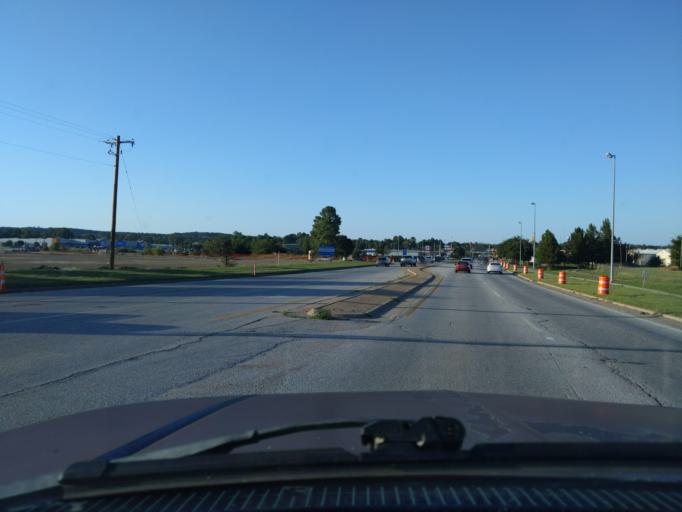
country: US
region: Oklahoma
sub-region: Tulsa County
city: Sand Springs
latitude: 36.1301
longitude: -96.1161
